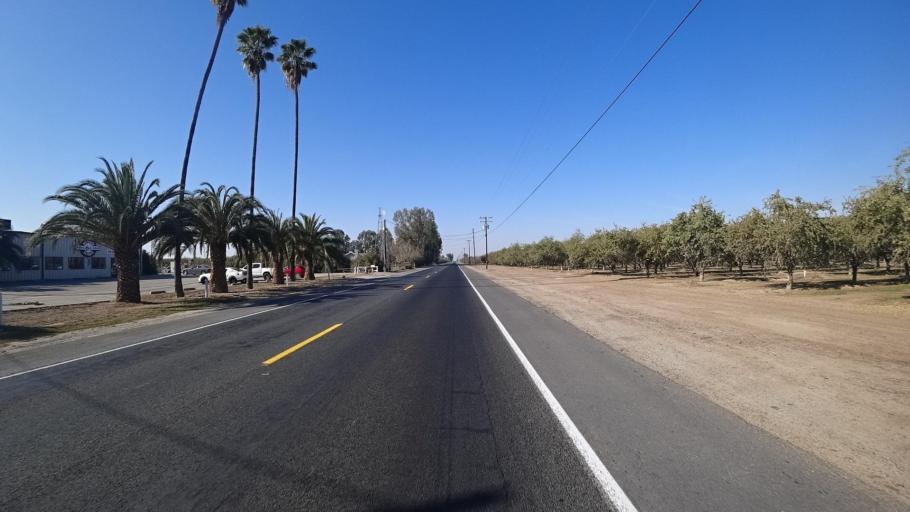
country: US
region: California
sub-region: Kern County
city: Delano
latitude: 35.7177
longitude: -119.3182
